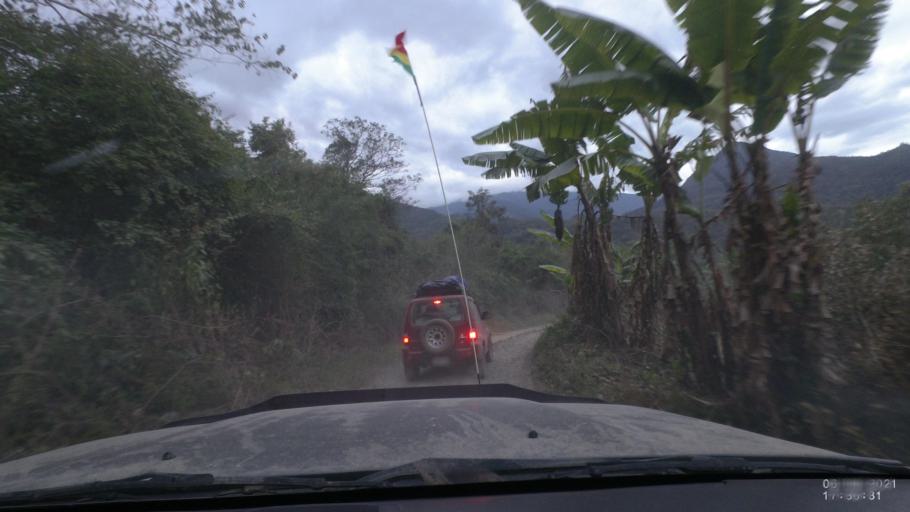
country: BO
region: La Paz
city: Quime
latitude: -16.4772
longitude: -66.7886
